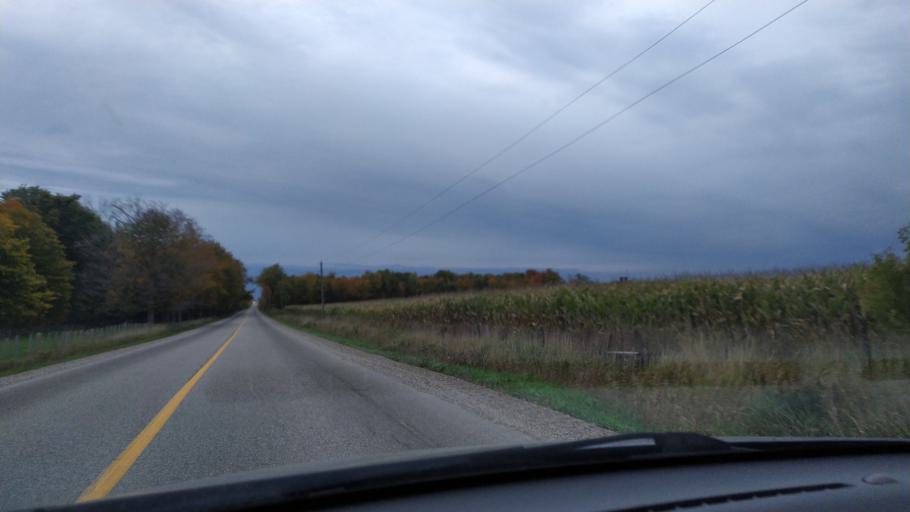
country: CA
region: Ontario
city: Waterloo
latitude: 43.5121
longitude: -80.7374
